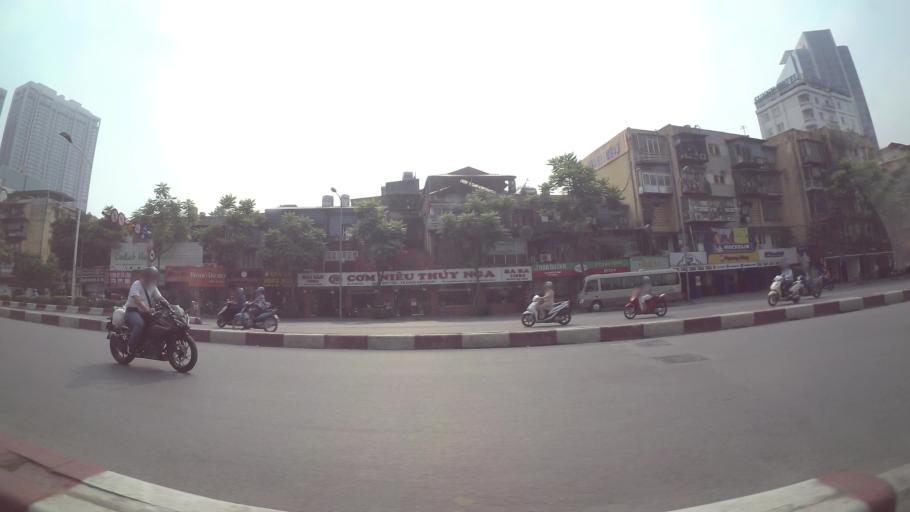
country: VN
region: Ha Noi
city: Cau Giay
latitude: 21.0285
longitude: 105.8123
